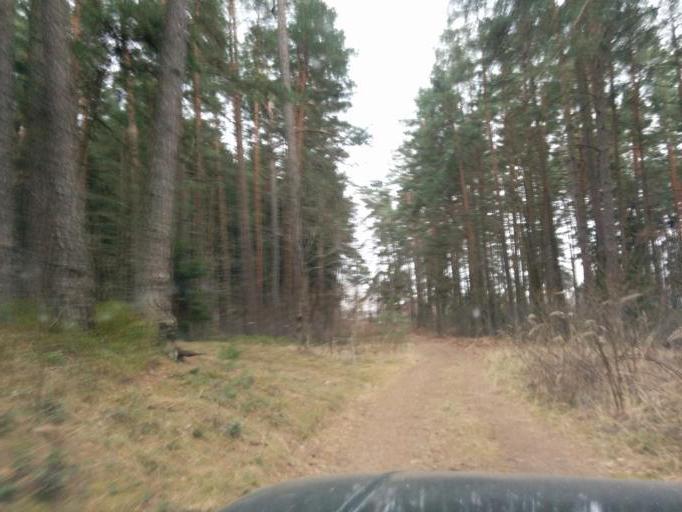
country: LV
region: Babite
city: Pinki
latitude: 56.9868
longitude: 23.8880
